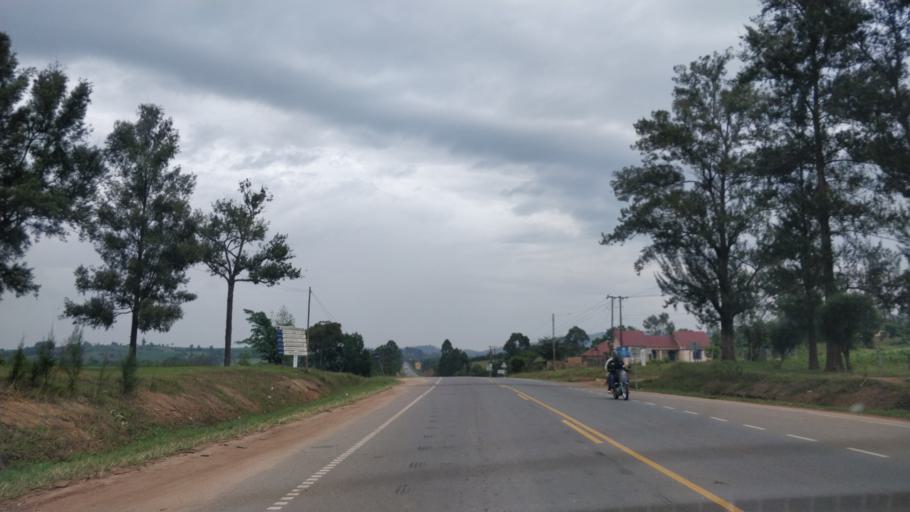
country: UG
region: Western Region
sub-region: Sheema District
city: Kibingo
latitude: -0.6586
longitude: 30.4661
